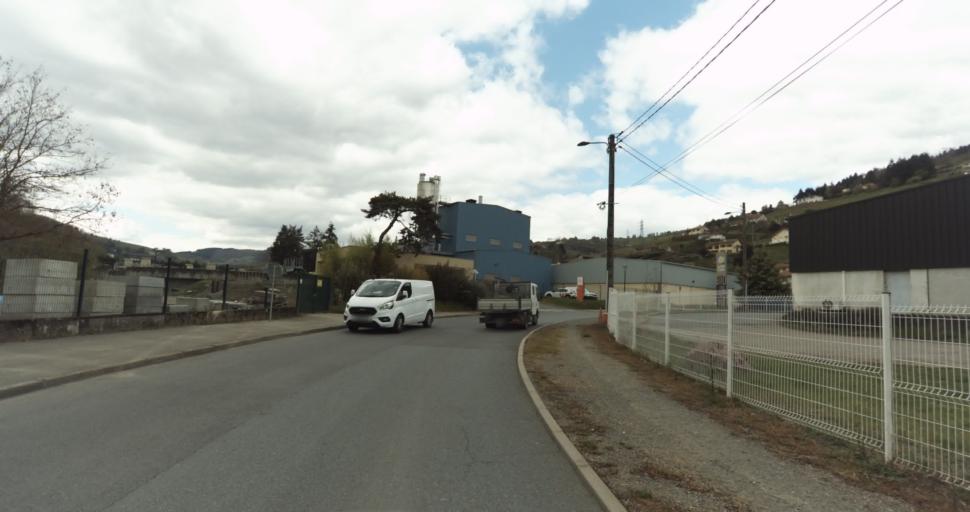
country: FR
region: Rhone-Alpes
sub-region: Departement du Rhone
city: Tarare
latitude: 45.8882
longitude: 4.4555
